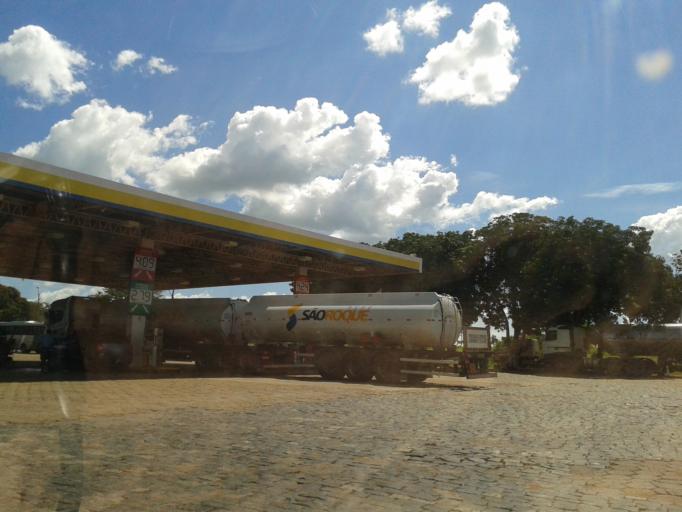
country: BR
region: Goias
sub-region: Pontalina
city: Pontalina
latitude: -17.5273
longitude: -49.2158
